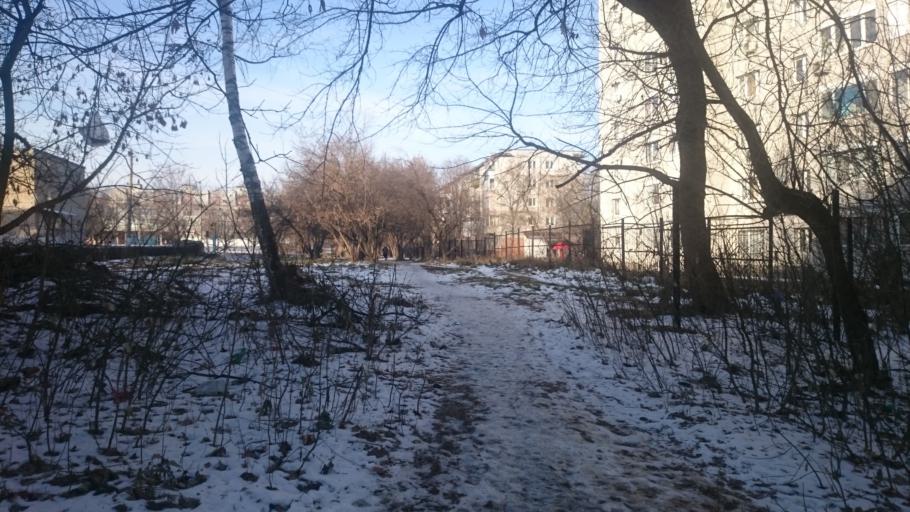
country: RU
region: Tula
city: Tula
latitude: 54.1759
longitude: 37.6394
